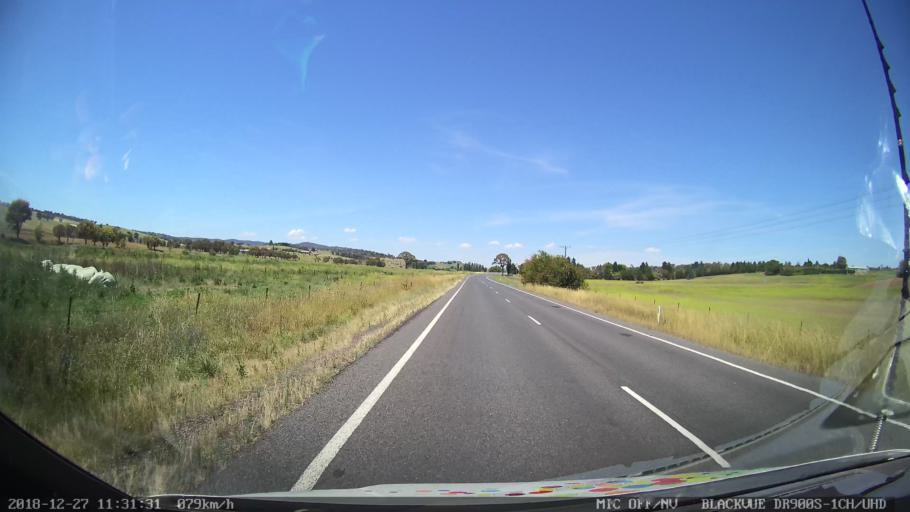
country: AU
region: New South Wales
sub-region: Bathurst Regional
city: Perthville
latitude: -33.4962
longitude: 149.5389
